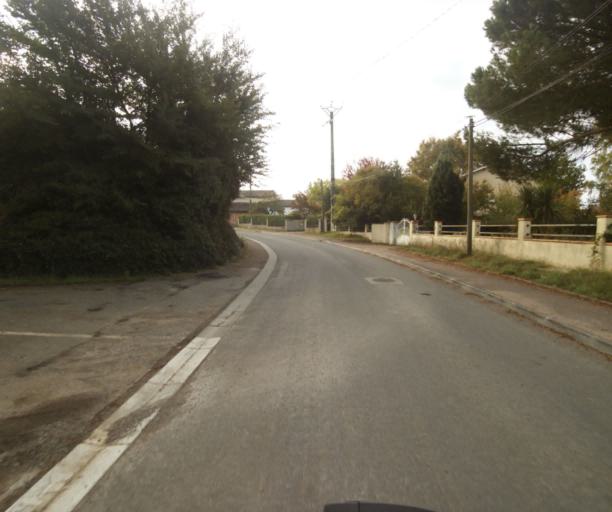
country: FR
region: Midi-Pyrenees
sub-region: Departement du Tarn-et-Garonne
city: Montech
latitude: 43.9632
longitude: 1.2268
